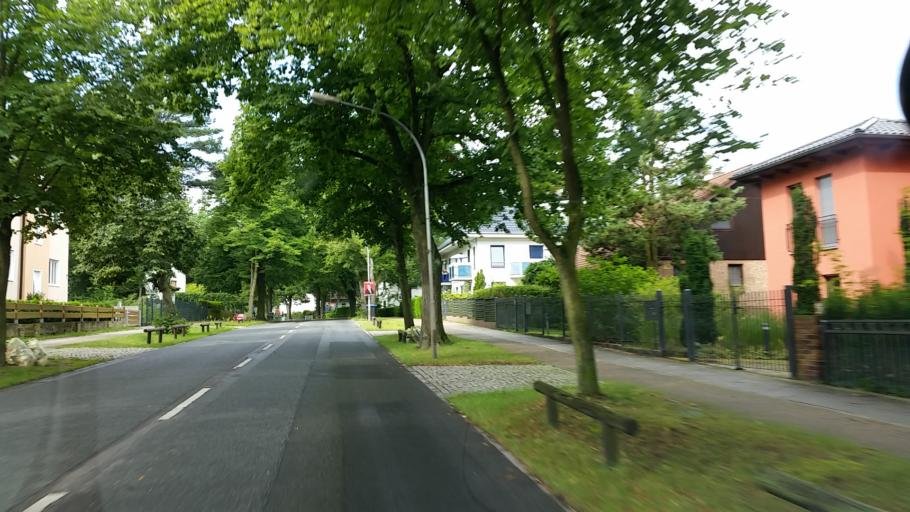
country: DE
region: Berlin
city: Lubars
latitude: 52.6343
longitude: 13.3476
